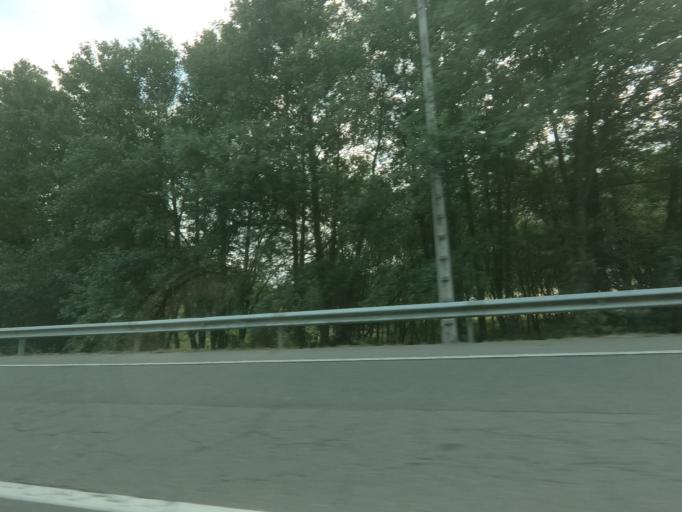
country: ES
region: Galicia
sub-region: Provincia de Ourense
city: Taboadela
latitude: 42.2621
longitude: -7.8338
